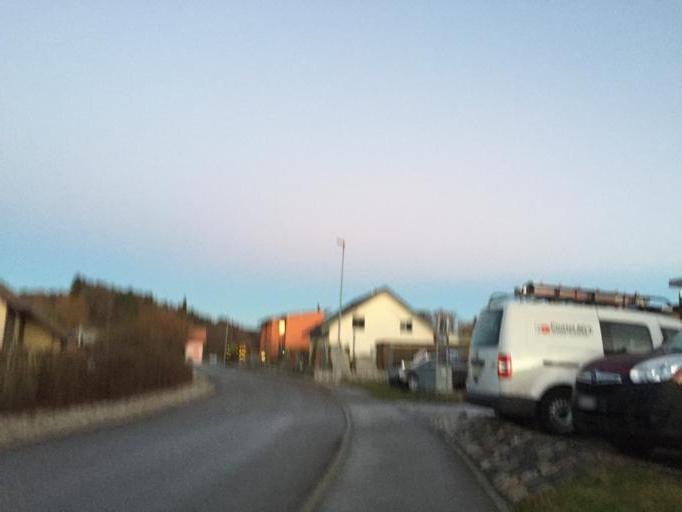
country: CH
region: Fribourg
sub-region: Sense District
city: Heitenried
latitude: 46.8271
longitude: 7.3071
